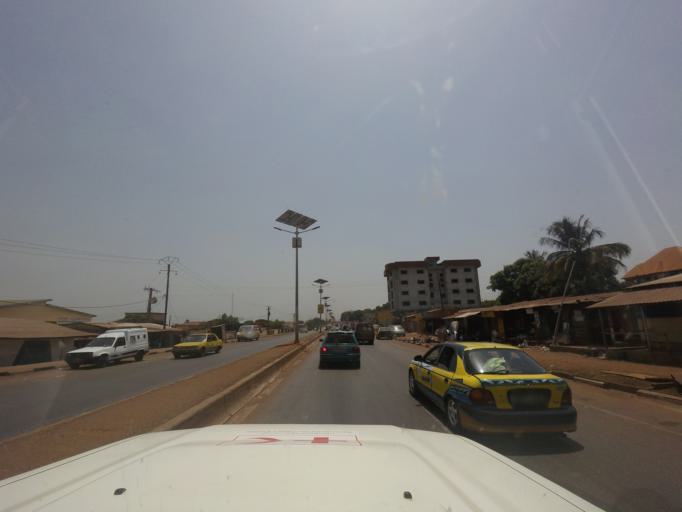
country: GN
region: Conakry
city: Conakry
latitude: 9.6316
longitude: -13.5738
